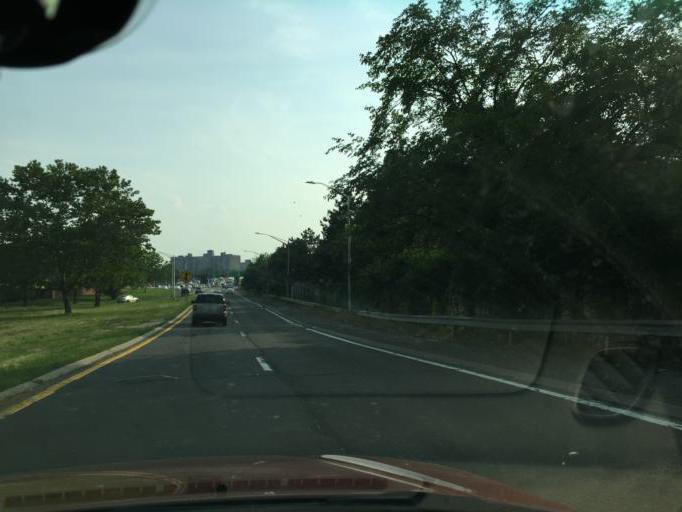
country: US
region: New York
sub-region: Queens County
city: Jamaica
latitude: 40.7438
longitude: -73.8394
